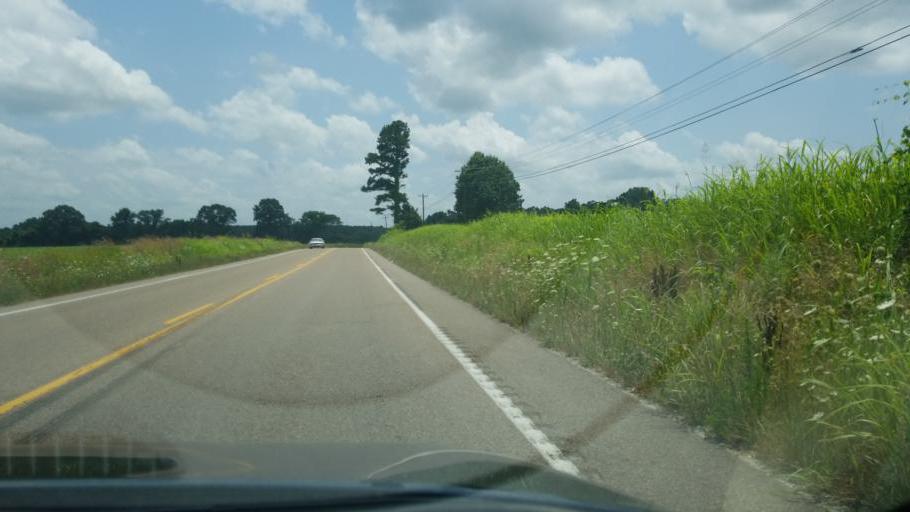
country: US
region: Tennessee
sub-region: Gibson County
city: Medina
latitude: 35.7174
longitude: -88.7170
